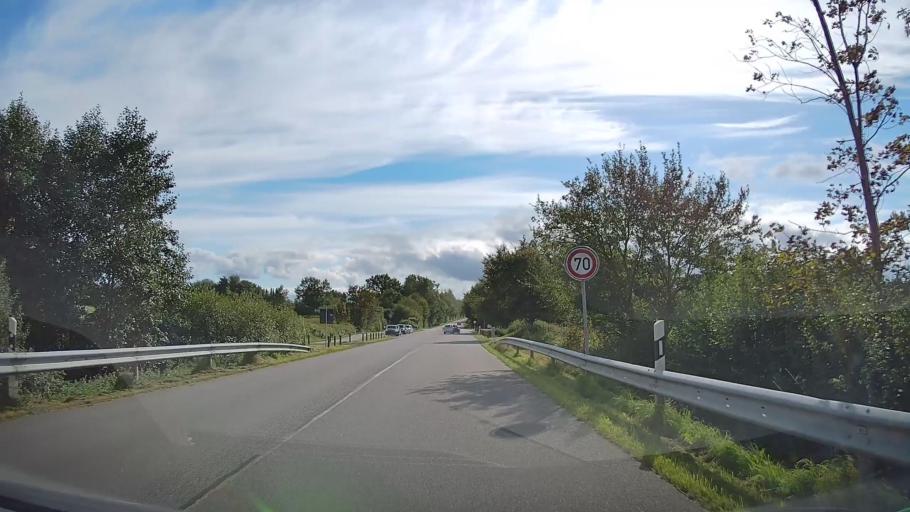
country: DE
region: Schleswig-Holstein
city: Glucksburg
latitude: 54.8525
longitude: 9.5868
